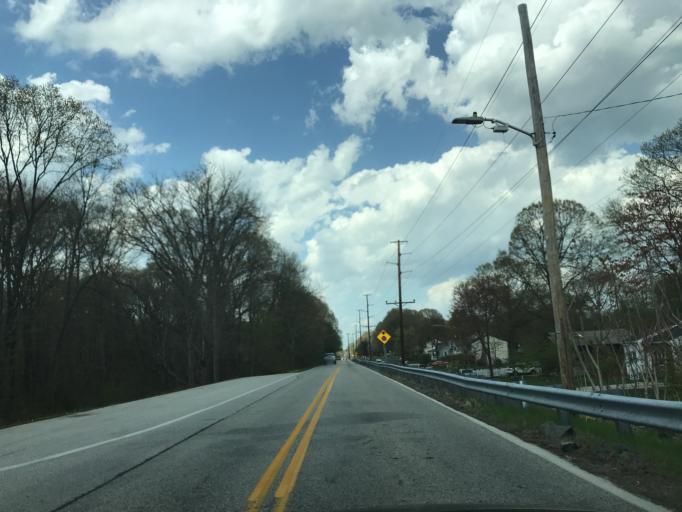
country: US
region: Maryland
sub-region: Anne Arundel County
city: Severn
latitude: 39.1401
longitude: -76.6717
